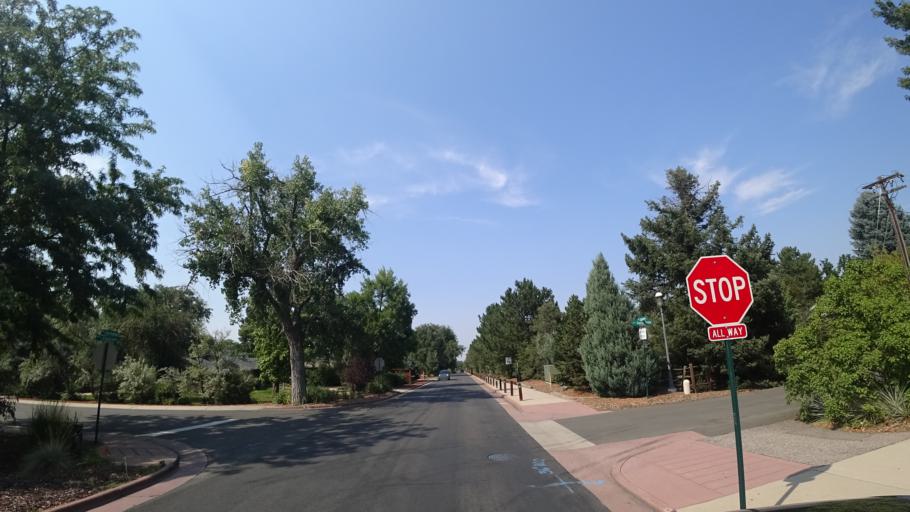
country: US
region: Colorado
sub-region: Arapahoe County
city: Greenwood Village
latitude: 39.6186
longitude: -104.9786
